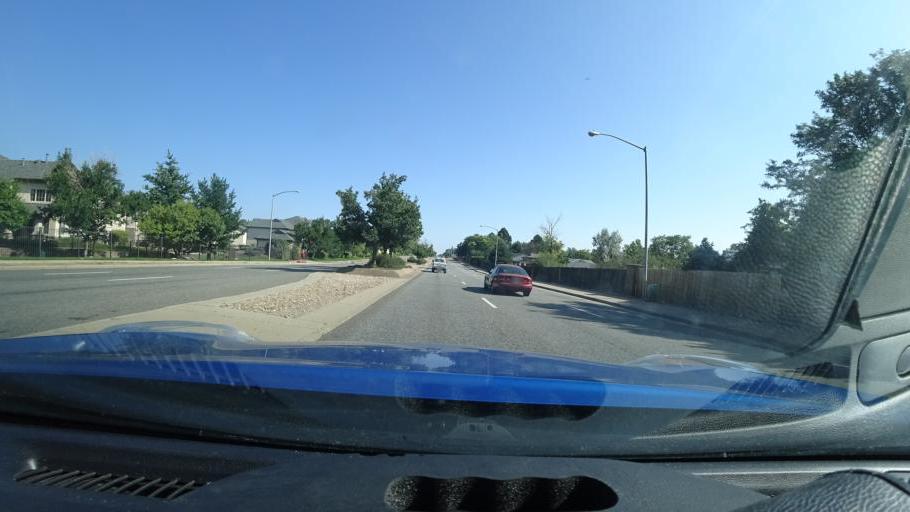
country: US
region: Colorado
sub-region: Adams County
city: Aurora
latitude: 39.6896
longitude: -104.8098
